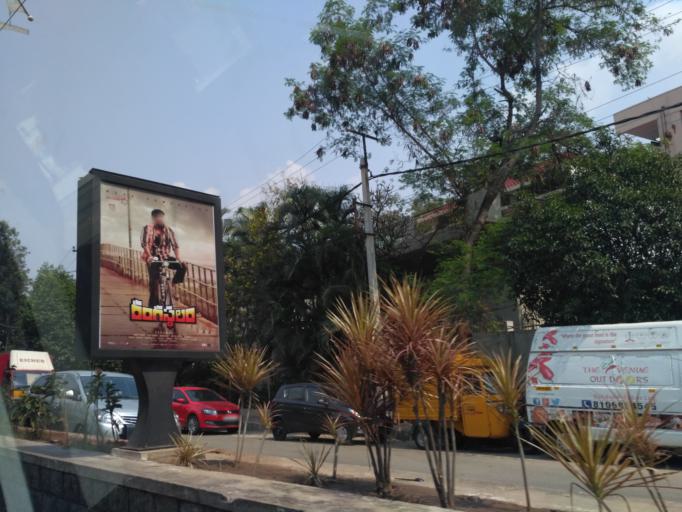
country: IN
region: Telangana
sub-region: Rangareddi
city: Kukatpalli
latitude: 17.4353
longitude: 78.4107
